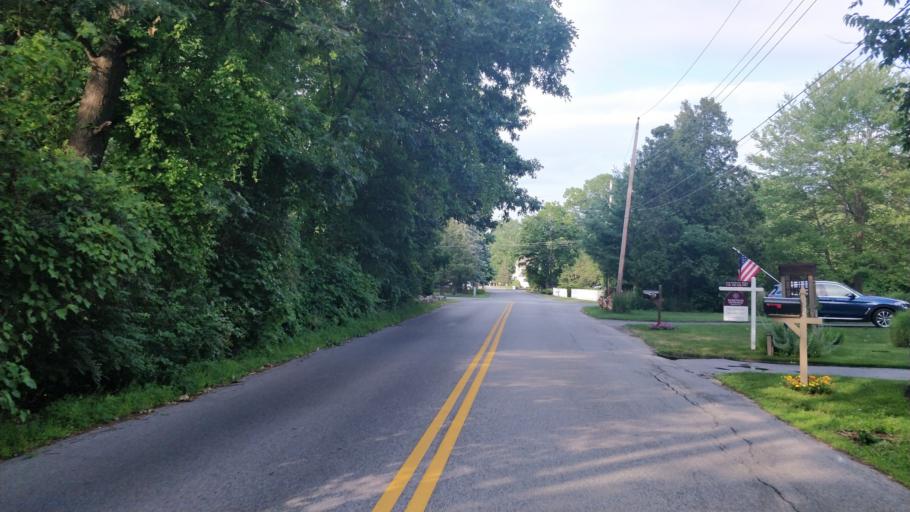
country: US
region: New York
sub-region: Saratoga County
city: Saratoga Springs
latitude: 43.0664
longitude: -73.7829
